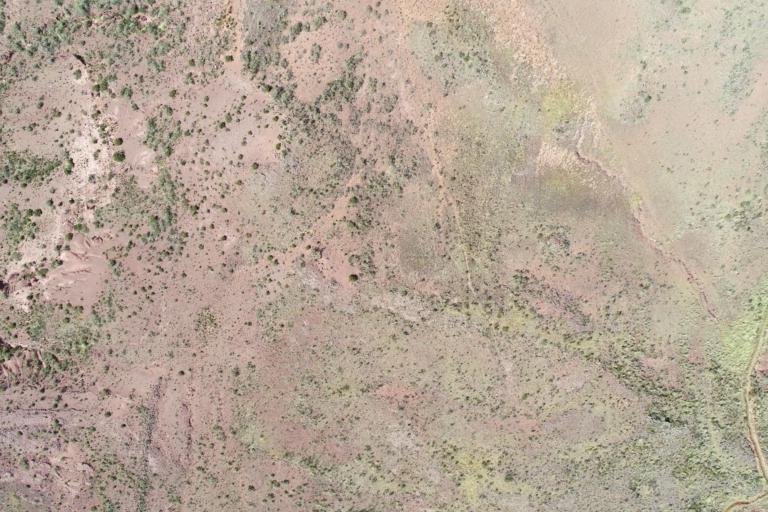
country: BO
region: La Paz
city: Tiahuanaco
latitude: -16.6024
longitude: -68.7569
